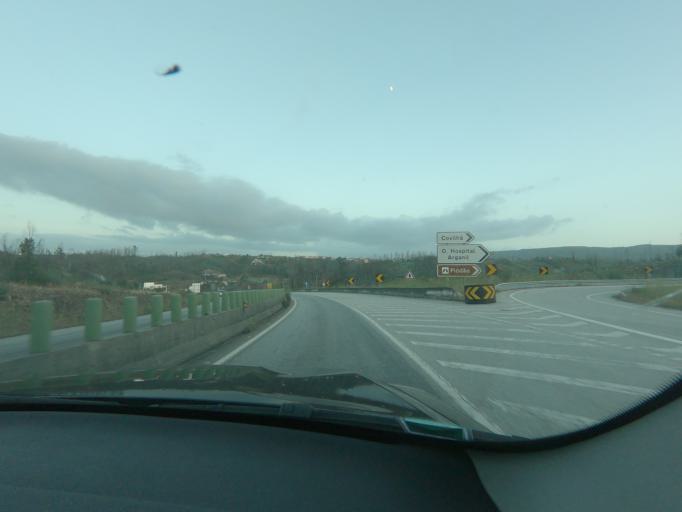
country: PT
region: Coimbra
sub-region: Penacova
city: Penacova
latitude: 40.3090
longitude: -8.2350
